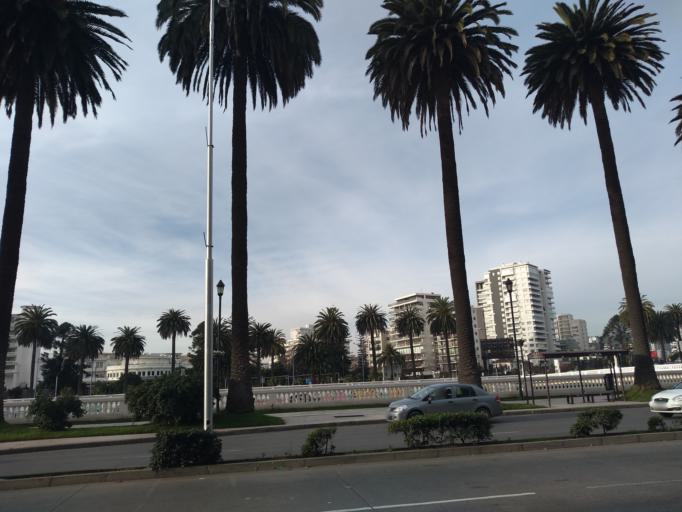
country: CL
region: Valparaiso
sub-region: Provincia de Valparaiso
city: Vina del Mar
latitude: -33.0208
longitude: -71.5619
